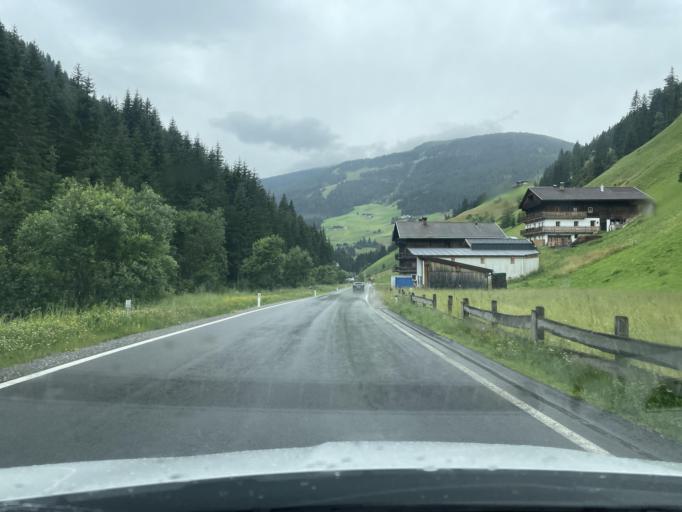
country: AT
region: Tyrol
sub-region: Politischer Bezirk Lienz
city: Ausservillgraten
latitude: 46.7927
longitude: 12.4424
